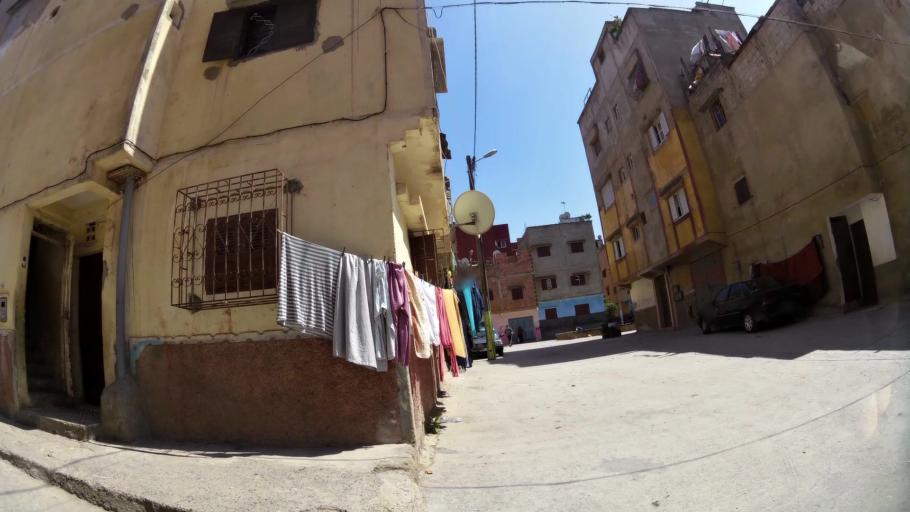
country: MA
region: Rabat-Sale-Zemmour-Zaer
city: Sale
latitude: 34.0617
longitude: -6.7787
